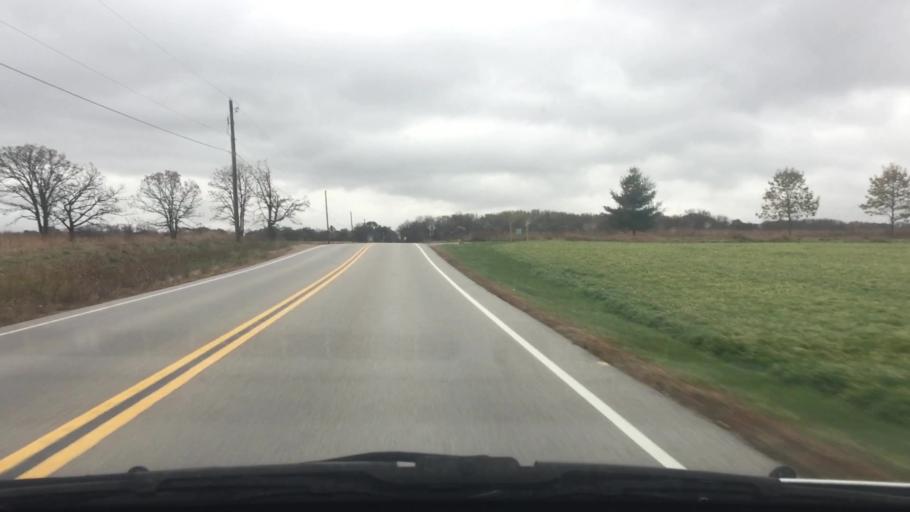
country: US
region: Wisconsin
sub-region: Waukesha County
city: Eagle
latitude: 42.8932
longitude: -88.4737
